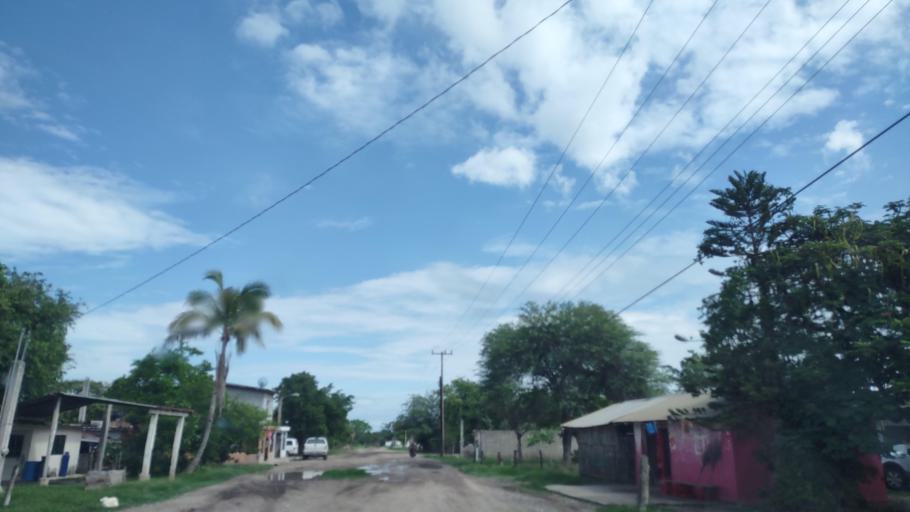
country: MX
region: Veracruz
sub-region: Panuco
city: Oviedo
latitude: 22.0019
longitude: -98.4563
